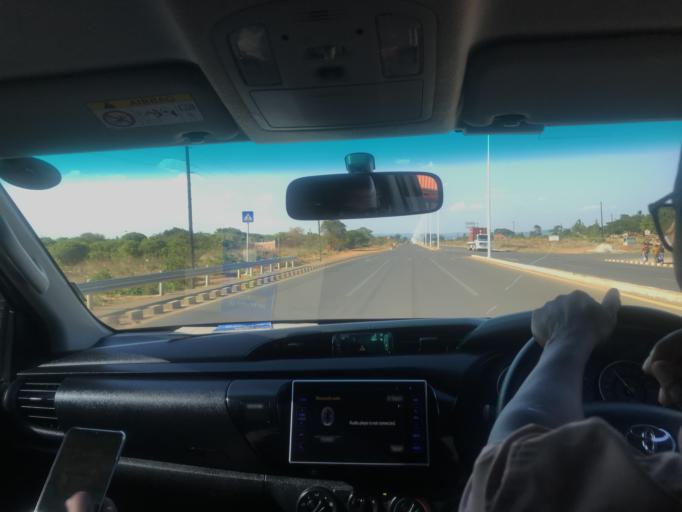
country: ZM
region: Northern
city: Mpika
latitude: -11.8268
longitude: 31.4487
